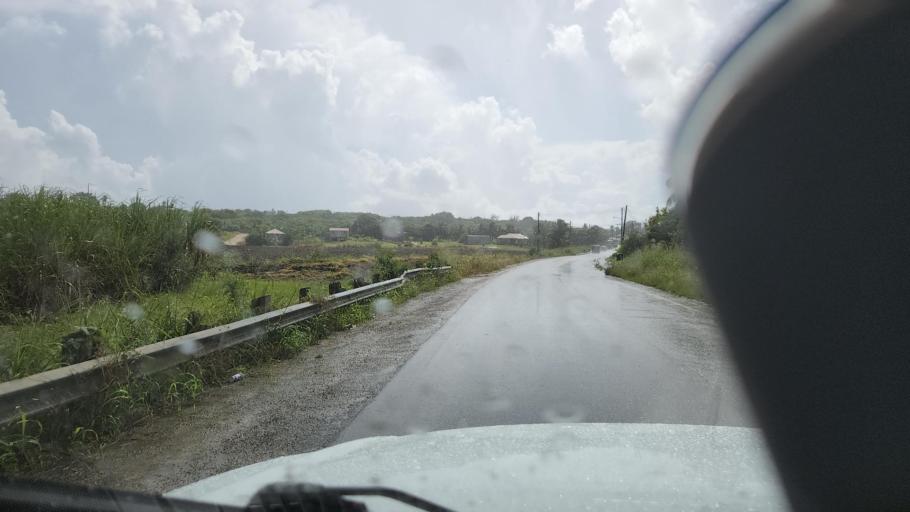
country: BB
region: Saint Michael
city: Bridgetown
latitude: 13.1154
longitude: -59.5631
